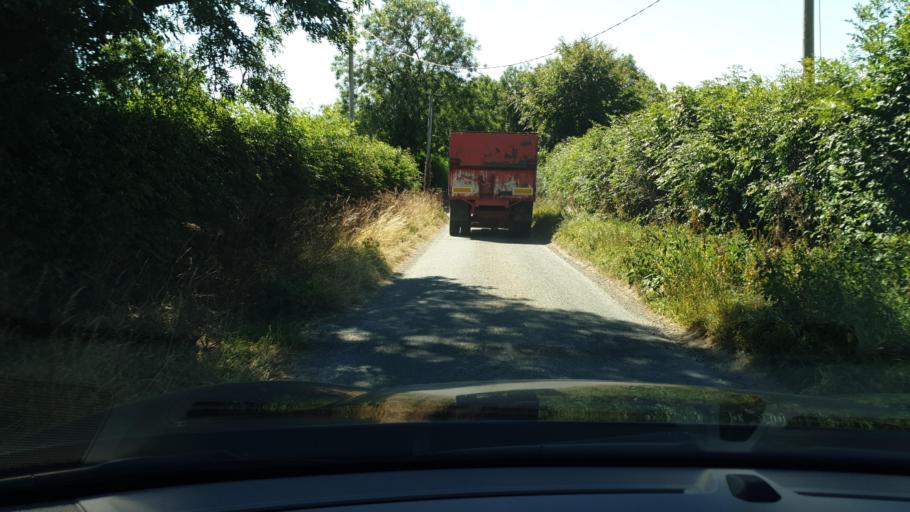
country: IE
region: Leinster
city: Hartstown
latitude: 53.4511
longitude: -6.4270
